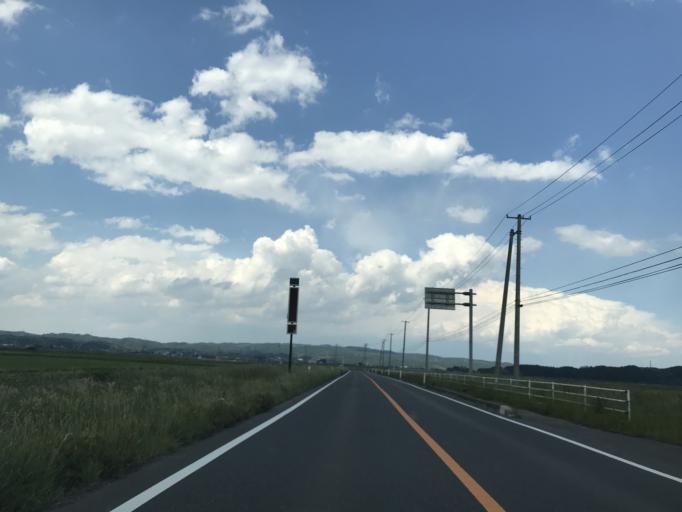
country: JP
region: Miyagi
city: Wakuya
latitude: 38.5127
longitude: 141.1241
